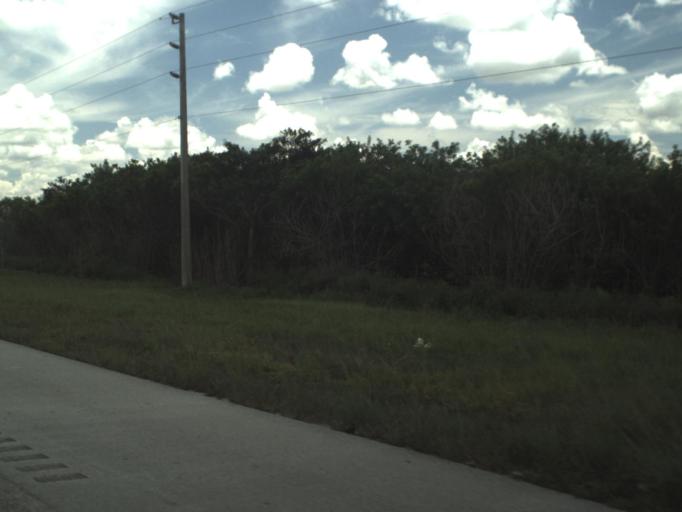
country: US
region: Florida
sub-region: Broward County
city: Weston
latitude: 26.1648
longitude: -80.8191
